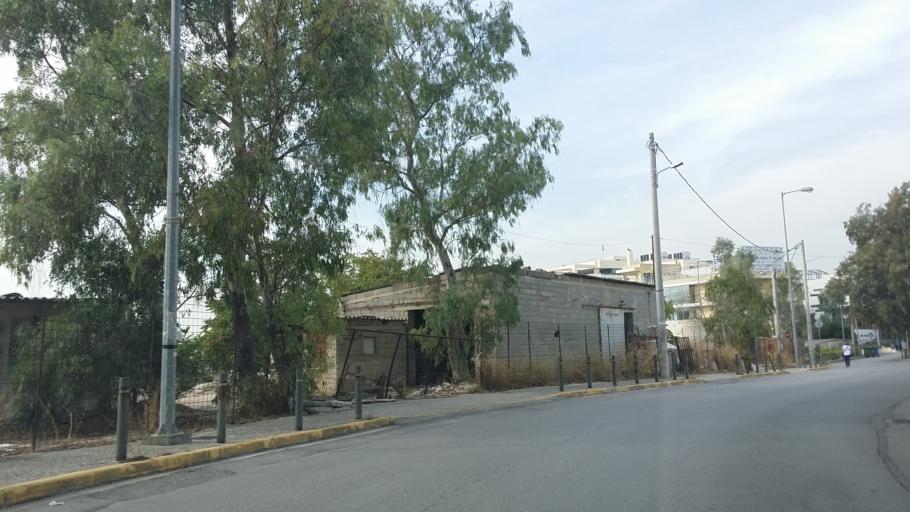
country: GR
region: Attica
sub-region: Nomarchia Athinas
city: Filothei
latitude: 38.0303
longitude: 23.7908
